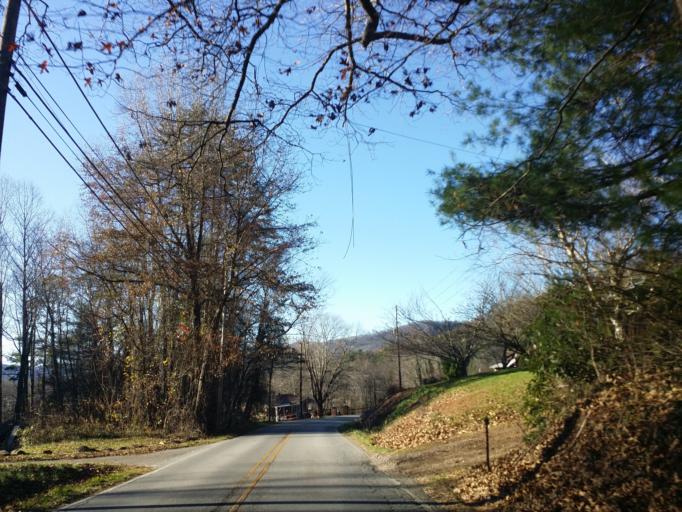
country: US
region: North Carolina
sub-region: Buncombe County
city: Swannanoa
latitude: 35.6079
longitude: -82.4128
